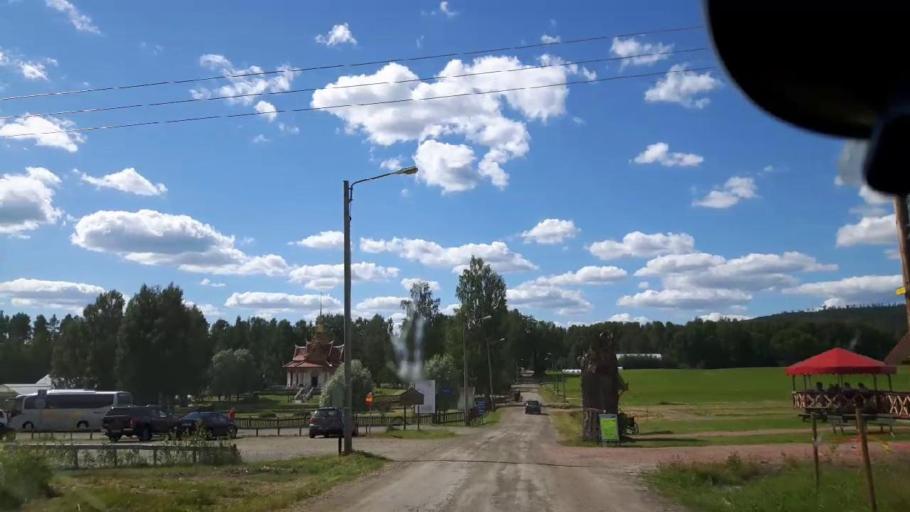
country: SE
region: Jaemtland
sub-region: Ragunda Kommun
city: Hammarstrand
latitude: 62.9567
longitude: 16.6783
